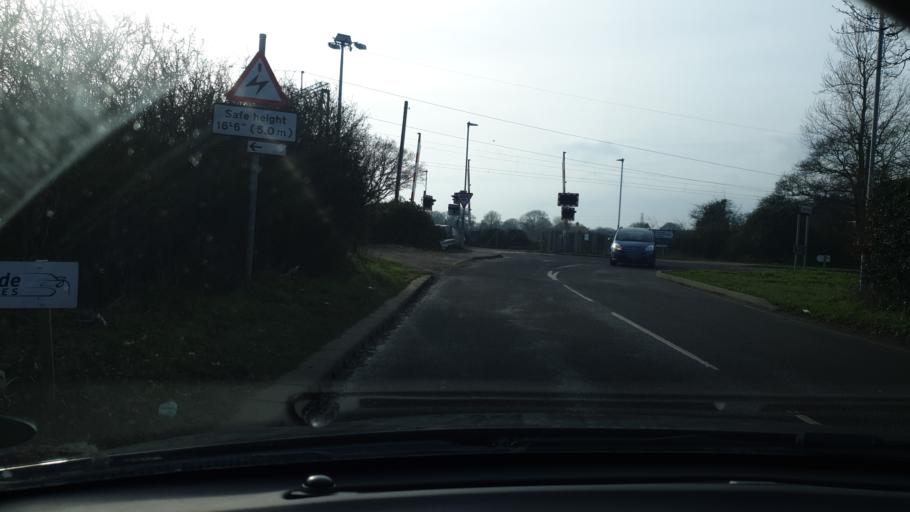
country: GB
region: England
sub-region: Essex
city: Great Bentley
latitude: 51.8499
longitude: 1.0363
